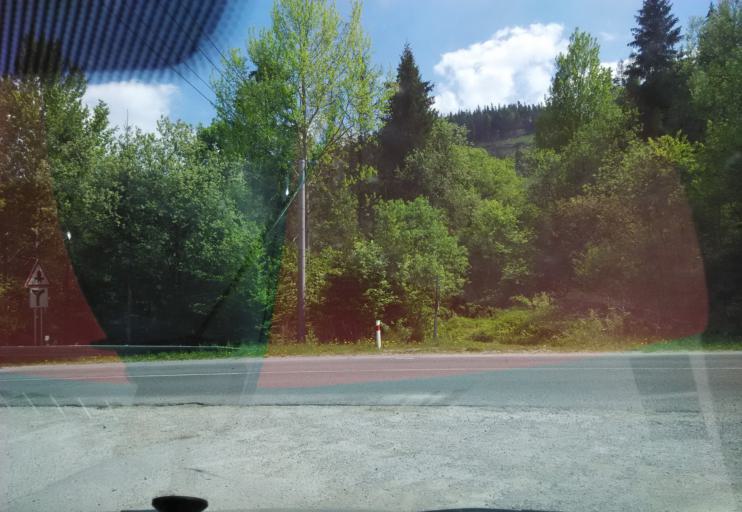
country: SK
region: Kosicky
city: Dobsina
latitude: 48.8534
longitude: 20.3844
